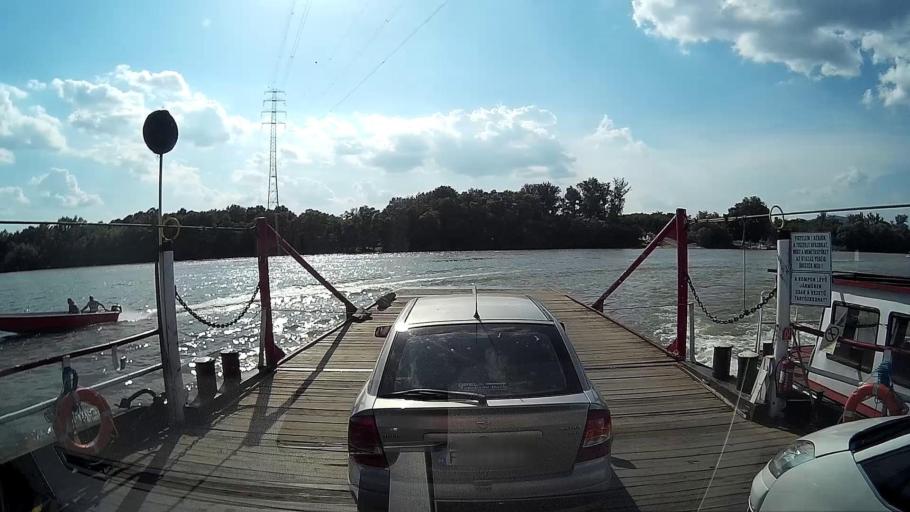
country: HU
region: Pest
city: God
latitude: 47.6586
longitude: 19.1161
